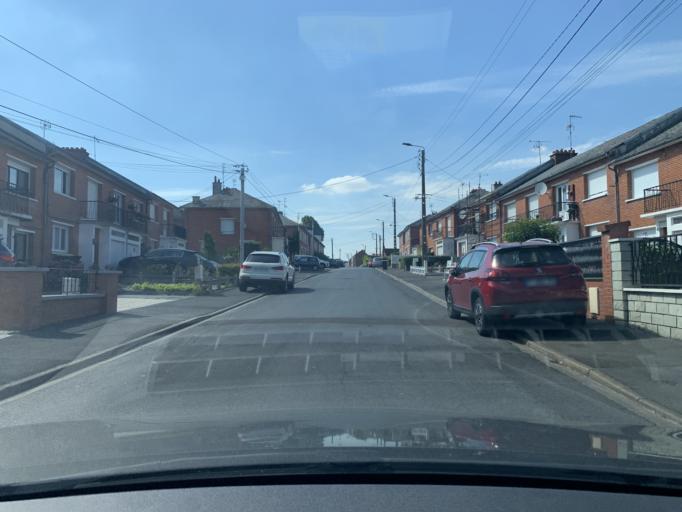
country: FR
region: Nord-Pas-de-Calais
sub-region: Departement du Nord
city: Cambrai
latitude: 50.1625
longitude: 3.2329
